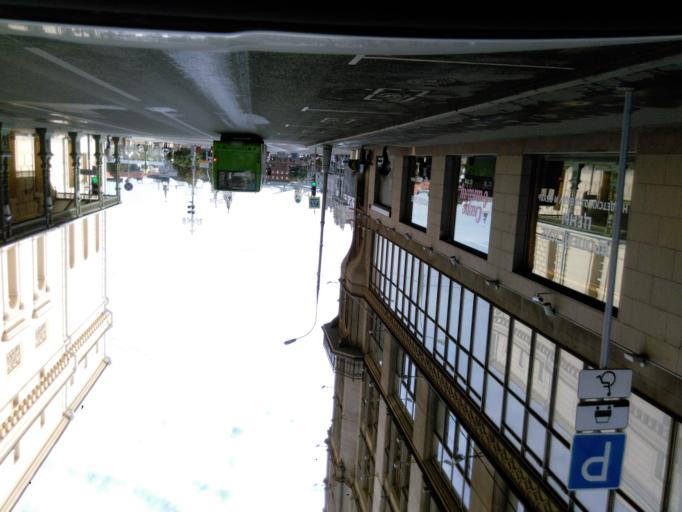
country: RU
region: Moscow
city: Moscow
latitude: 55.7605
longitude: 37.6192
